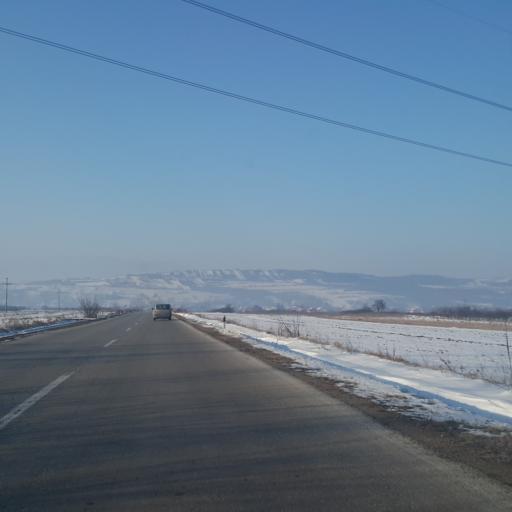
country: RS
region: Central Serbia
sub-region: Nisavski Okrug
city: Merosina
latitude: 43.2622
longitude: 21.6676
